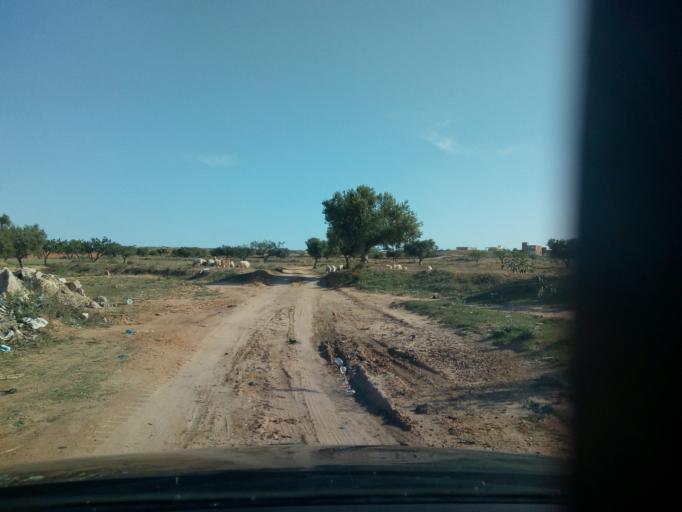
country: TN
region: Safaqis
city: Sfax
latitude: 34.7255
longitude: 10.6127
